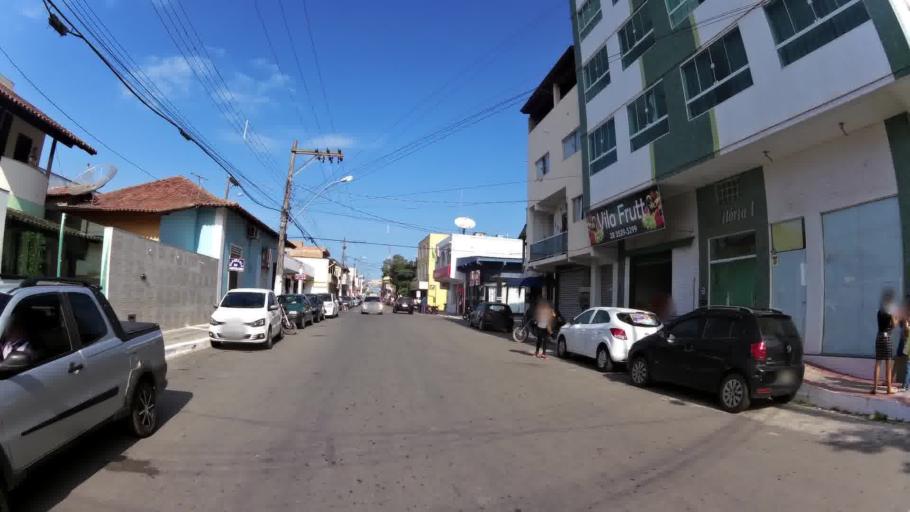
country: BR
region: Espirito Santo
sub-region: Itapemirim
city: Itapemirim
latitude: -21.0085
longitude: -40.8351
